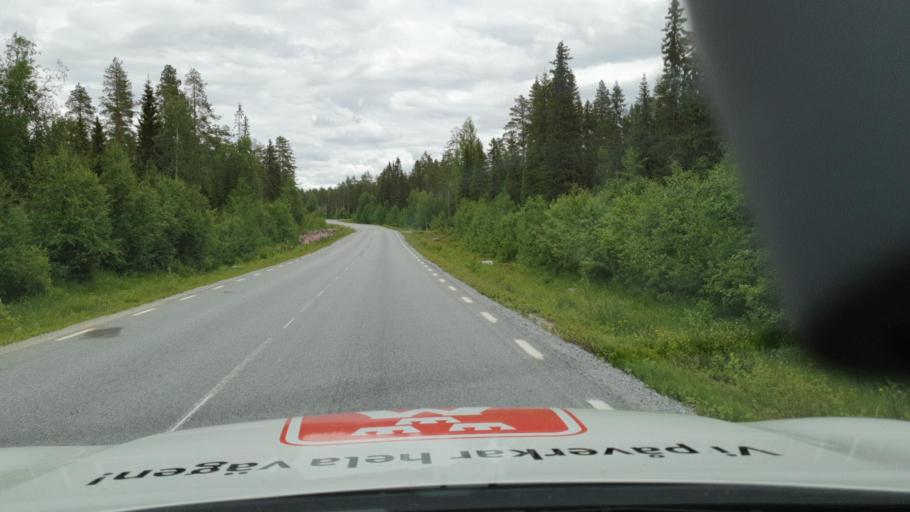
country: SE
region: Vaesterbotten
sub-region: Bjurholms Kommun
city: Bjurholm
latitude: 63.8823
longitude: 19.0531
